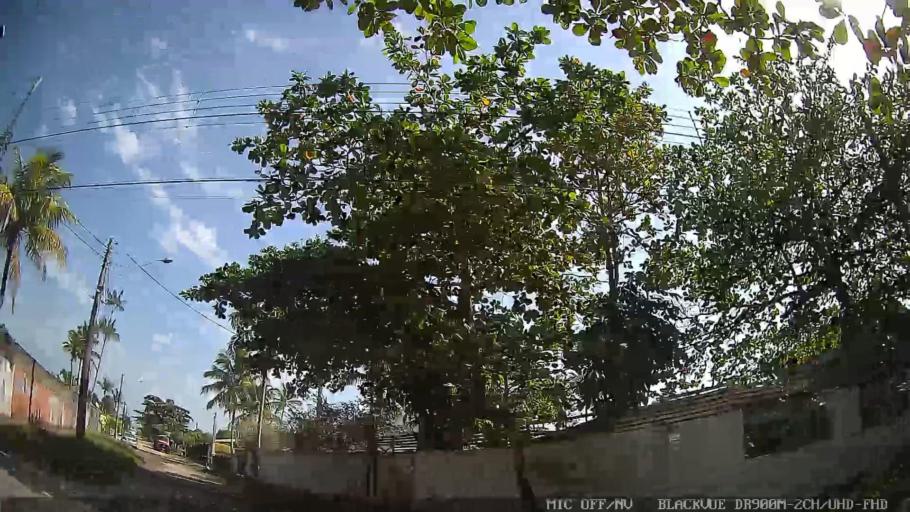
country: BR
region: Sao Paulo
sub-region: Guaruja
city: Guaruja
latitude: -23.9747
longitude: -46.1897
